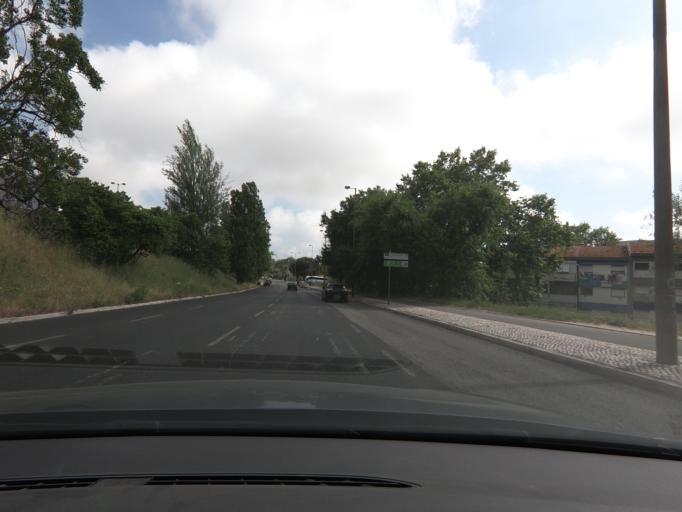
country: PT
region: Lisbon
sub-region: Loures
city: Moscavide
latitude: 38.7684
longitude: -9.1244
